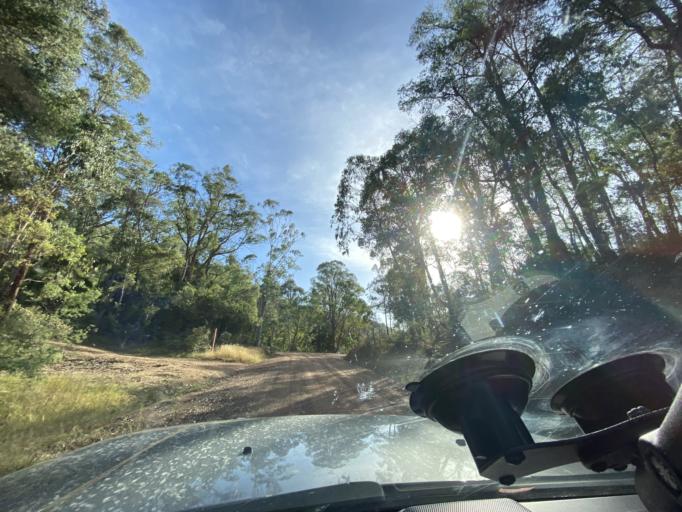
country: AU
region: Victoria
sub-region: Mansfield
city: Mansfield
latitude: -37.5166
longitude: 146.0950
